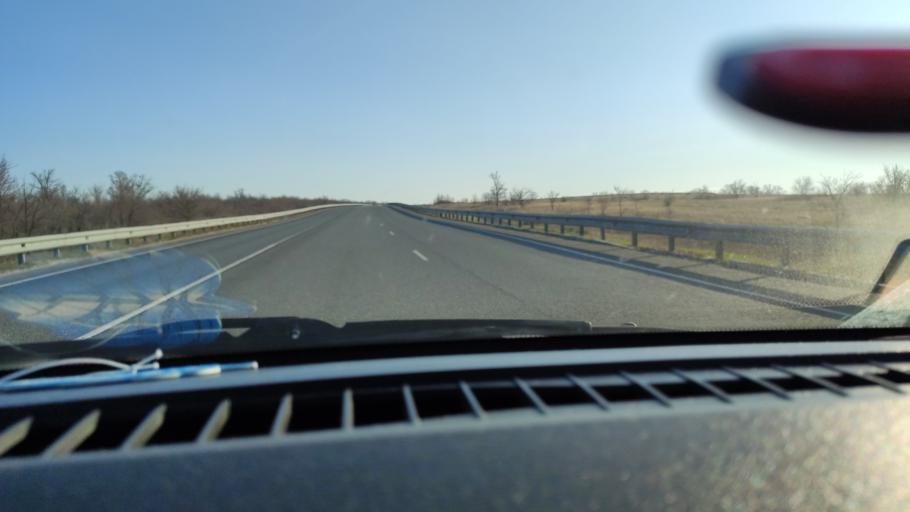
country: RU
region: Saratov
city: Balakovo
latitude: 52.2006
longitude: 47.8641
